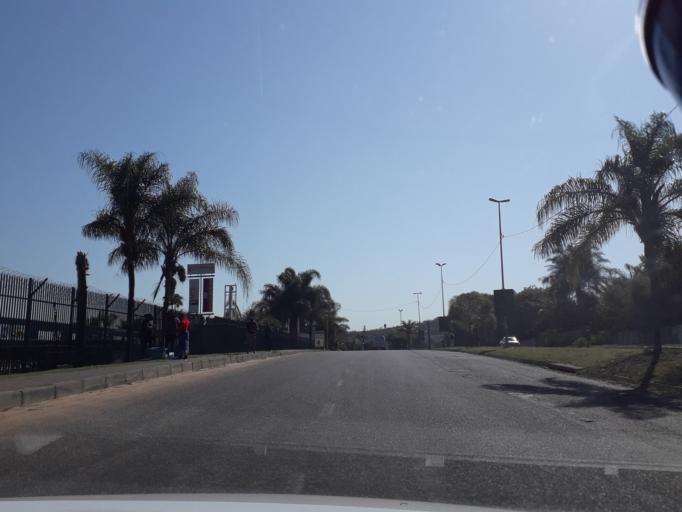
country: ZA
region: Gauteng
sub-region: City of Johannesburg Metropolitan Municipality
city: Roodepoort
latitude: -26.0969
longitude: 27.9427
